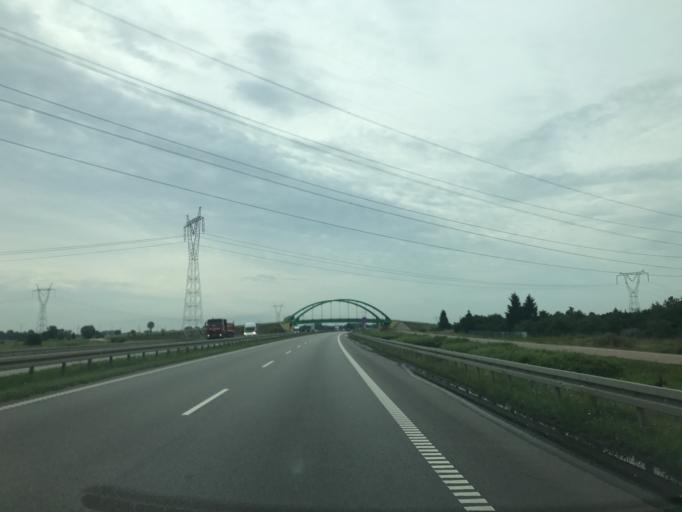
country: PL
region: Pomeranian Voivodeship
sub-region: Gdansk
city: Gdansk
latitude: 54.3359
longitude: 18.7023
